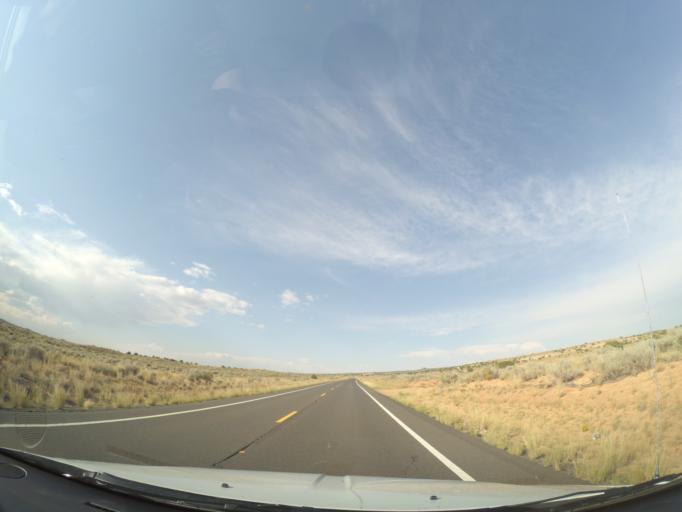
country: US
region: Arizona
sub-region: Coconino County
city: Kaibito
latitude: 36.4872
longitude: -111.4124
